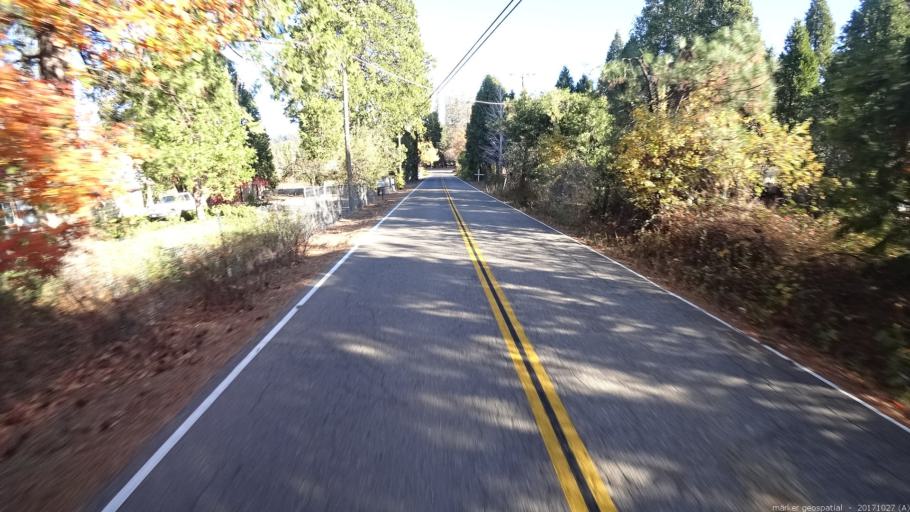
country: US
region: California
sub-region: Shasta County
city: Burney
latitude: 41.0130
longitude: -121.9063
